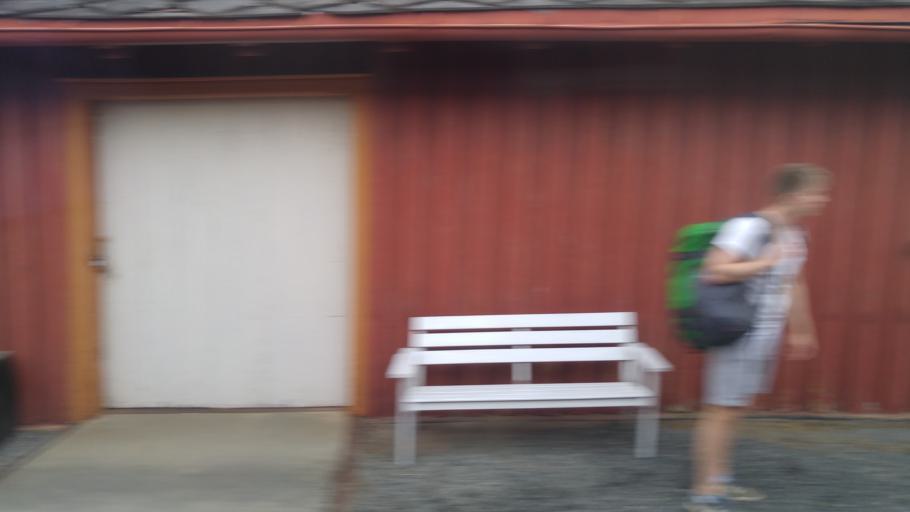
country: NO
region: Nord-Trondelag
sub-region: Meraker
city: Meraker
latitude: 63.4226
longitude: 11.7602
